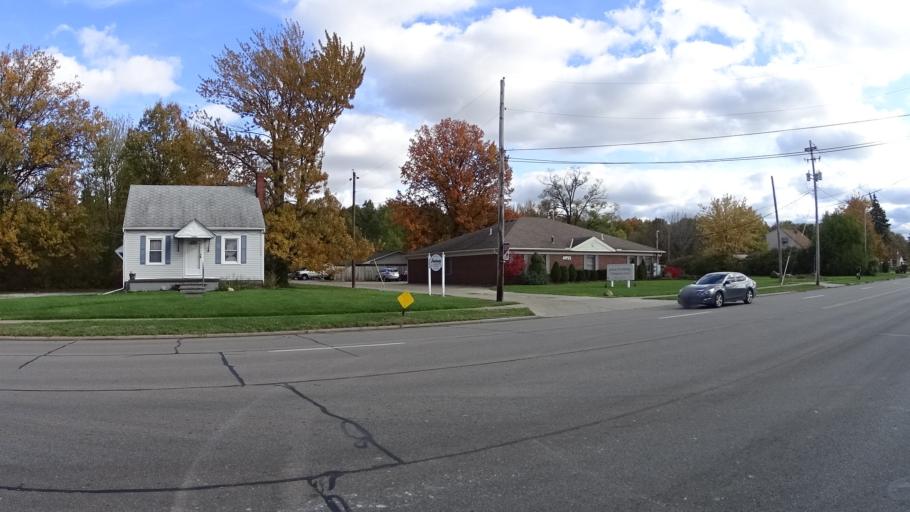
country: US
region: Ohio
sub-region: Lorain County
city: Lorain
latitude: 41.4244
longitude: -82.1857
